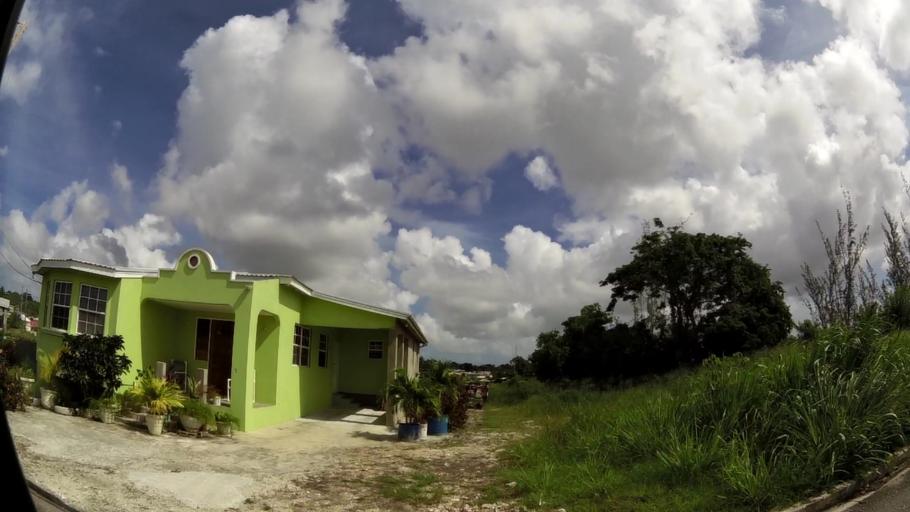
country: BB
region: Saint Michael
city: Bridgetown
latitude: 13.1241
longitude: -59.6134
